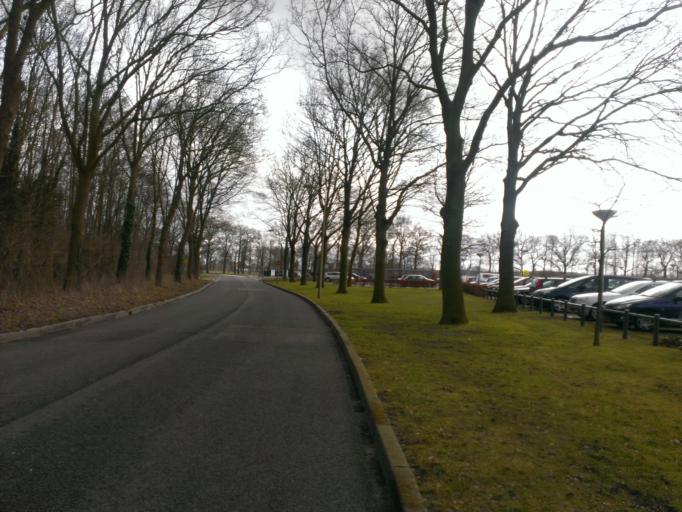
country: NL
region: Overijssel
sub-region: Gemeente Almelo
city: Almelo
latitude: 52.3374
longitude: 6.6960
